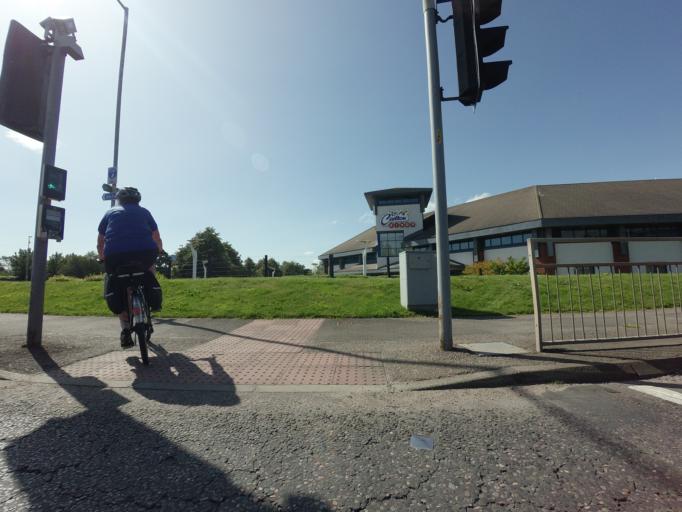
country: GB
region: Scotland
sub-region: Highland
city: Inverness
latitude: 57.4722
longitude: -4.1900
